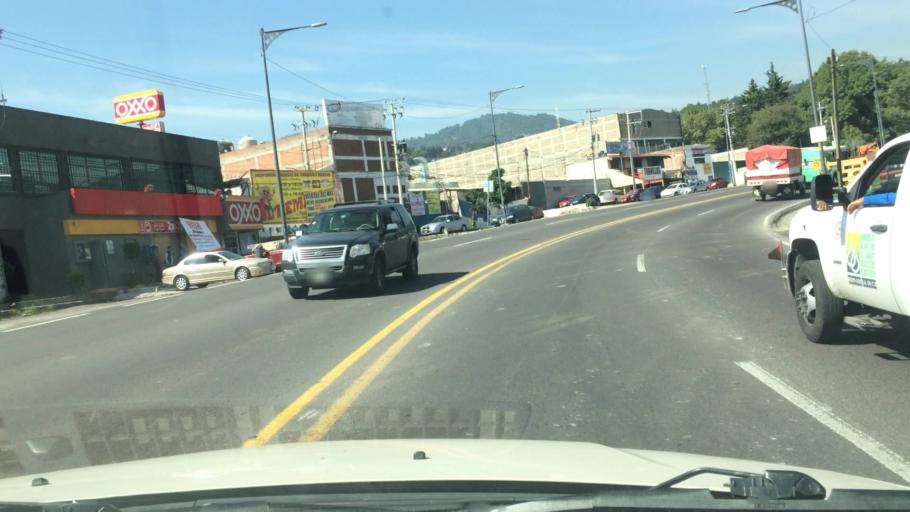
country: MX
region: Mexico City
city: Tlalpan
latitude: 19.2581
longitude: -99.1737
